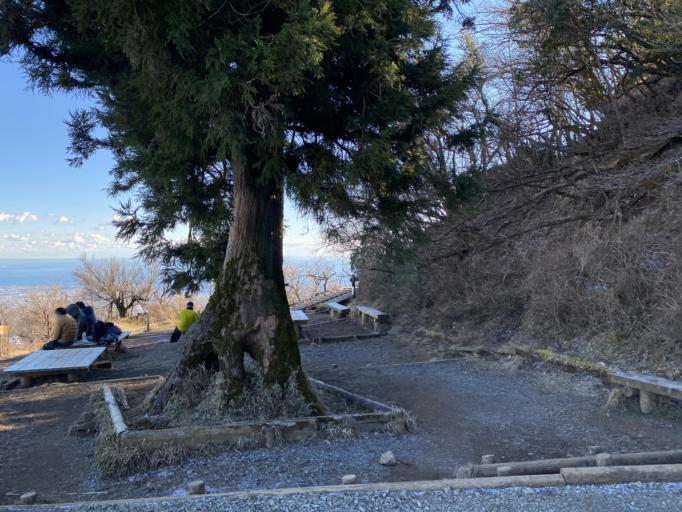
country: JP
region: Kanagawa
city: Hadano
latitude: 35.4410
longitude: 139.2315
